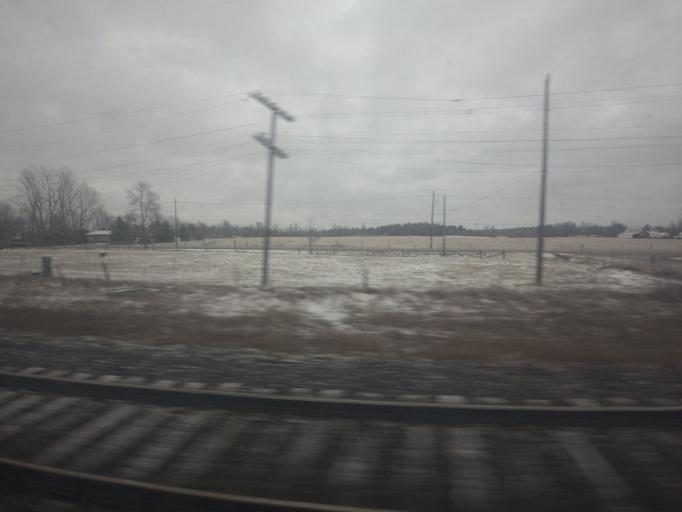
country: CA
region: Ontario
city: Gananoque
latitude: 44.3689
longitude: -76.1526
